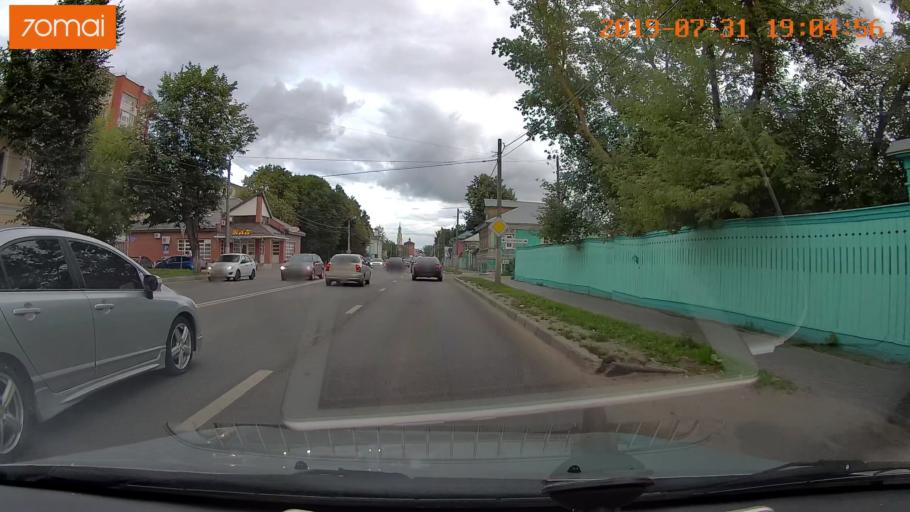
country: RU
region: Moskovskaya
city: Raduzhnyy
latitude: 55.1075
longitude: 38.7435
